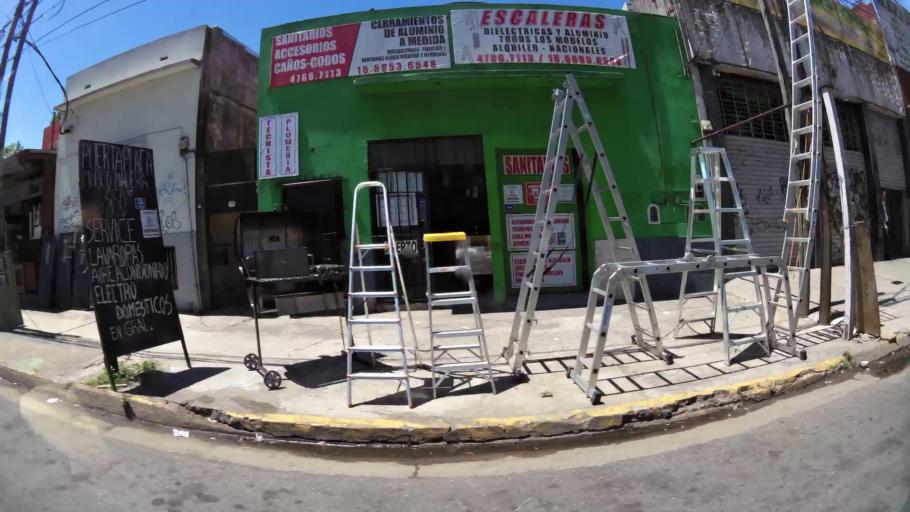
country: AR
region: Buenos Aires
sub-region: Partido de San Isidro
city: San Isidro
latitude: -34.5057
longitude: -58.5634
